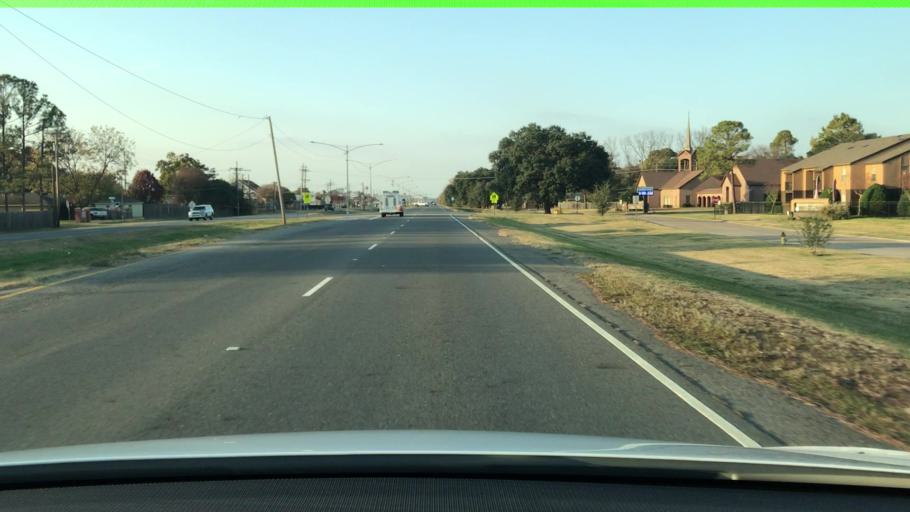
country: US
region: Louisiana
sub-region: Bossier Parish
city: Bossier City
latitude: 32.4161
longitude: -93.7026
